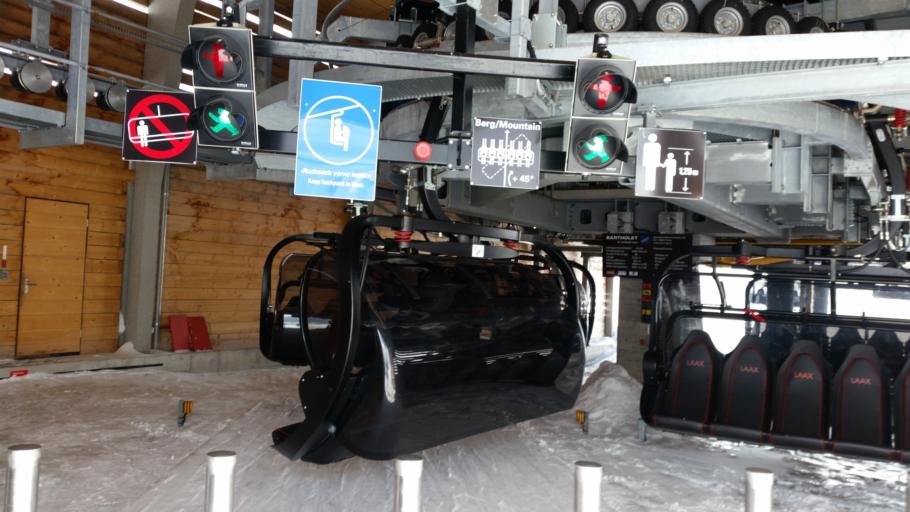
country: CH
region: Grisons
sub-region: Surselva District
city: Ilanz
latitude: 46.8426
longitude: 9.1561
